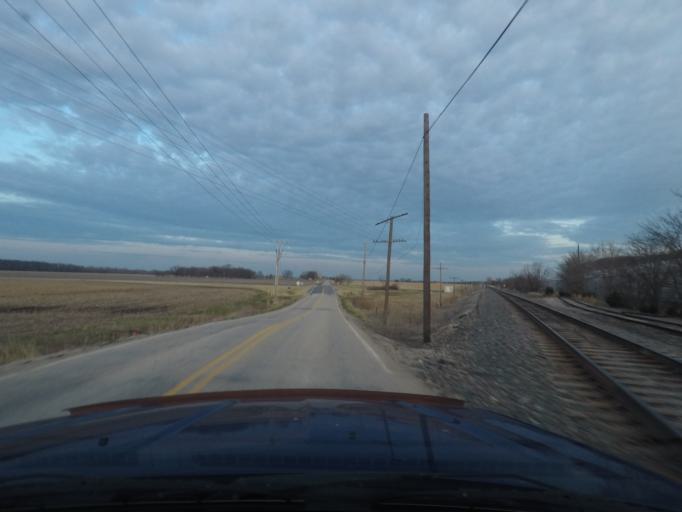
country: US
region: Kansas
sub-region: Douglas County
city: Lawrence
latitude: 38.9569
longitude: -95.2022
